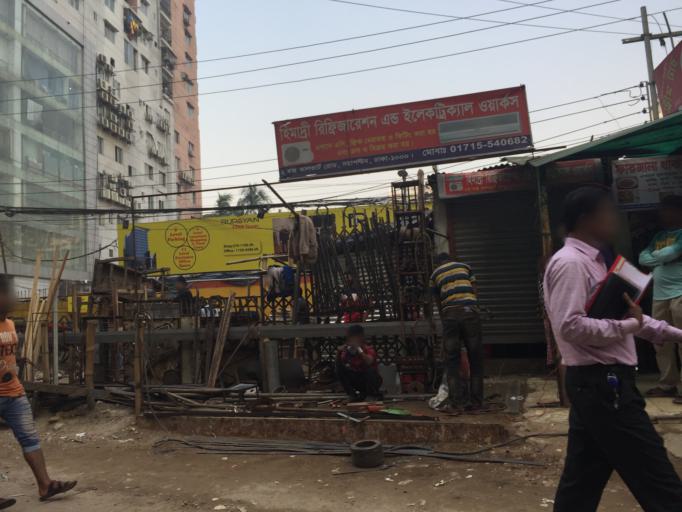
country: BD
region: Dhaka
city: Paltan
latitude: 23.7328
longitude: 90.4125
